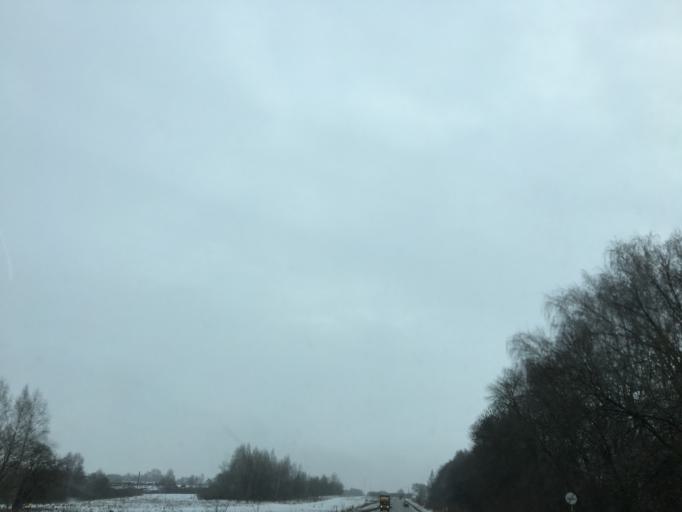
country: RU
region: Tula
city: Borodinskiy
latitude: 54.0315
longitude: 37.8812
